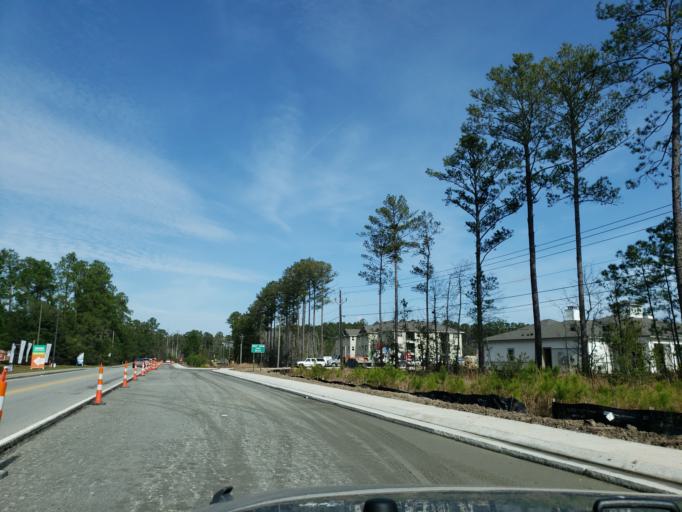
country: US
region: Georgia
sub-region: Chatham County
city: Pooler
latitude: 32.1702
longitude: -81.2339
